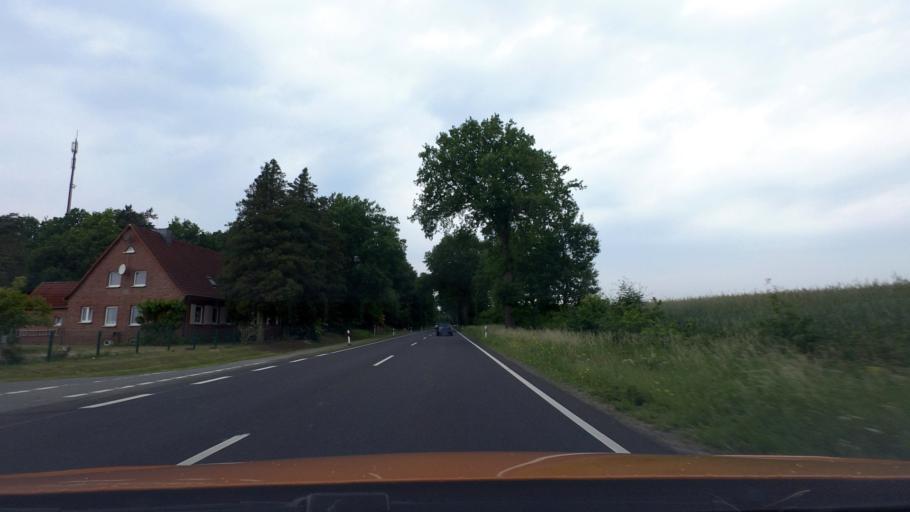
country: DE
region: Lower Saxony
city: Wietzen
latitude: 52.6854
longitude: 9.0989
